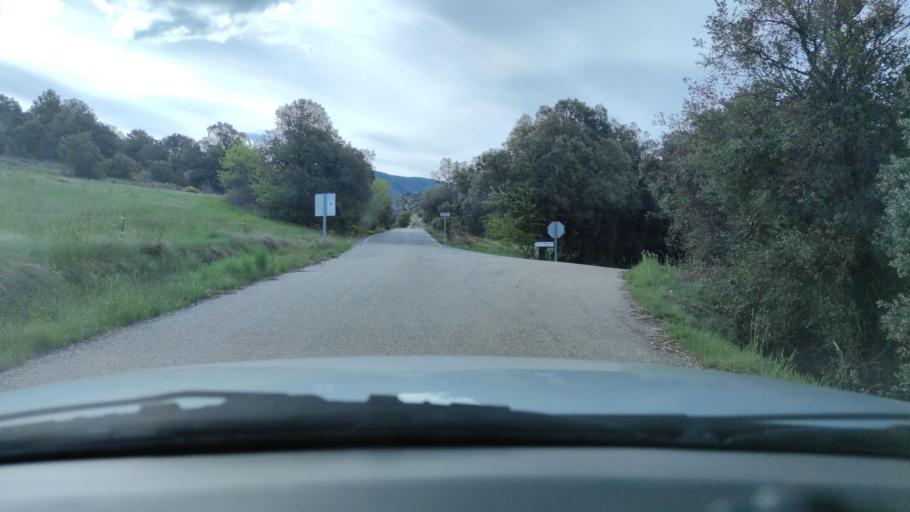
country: ES
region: Catalonia
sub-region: Provincia de Lleida
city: Coll de Nargo
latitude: 42.2327
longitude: 1.3979
